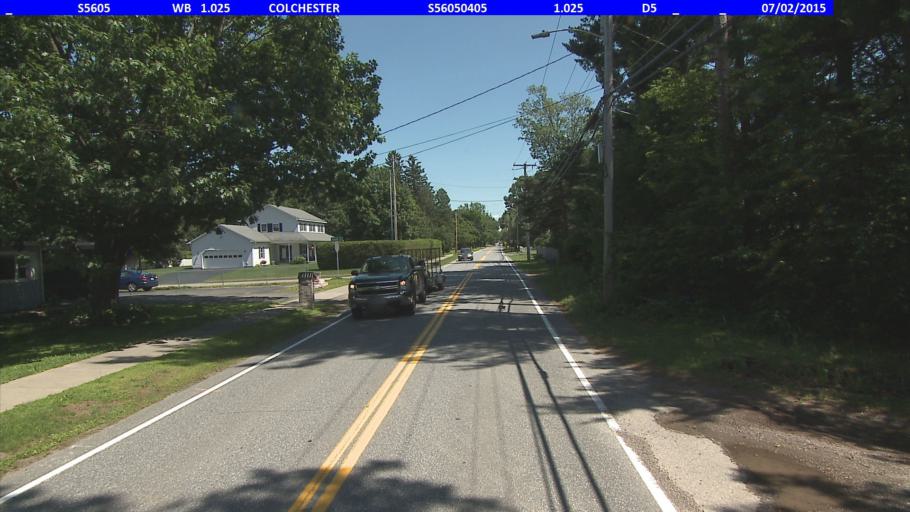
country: US
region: Vermont
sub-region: Chittenden County
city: Burlington
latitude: 44.5451
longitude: -73.2653
